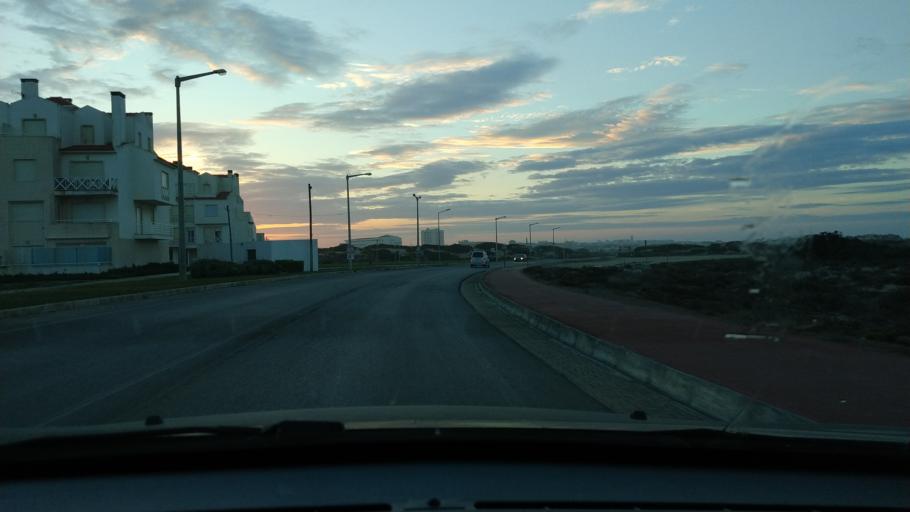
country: PT
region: Leiria
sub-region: Peniche
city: Peniche
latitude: 39.3568
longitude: -9.3553
